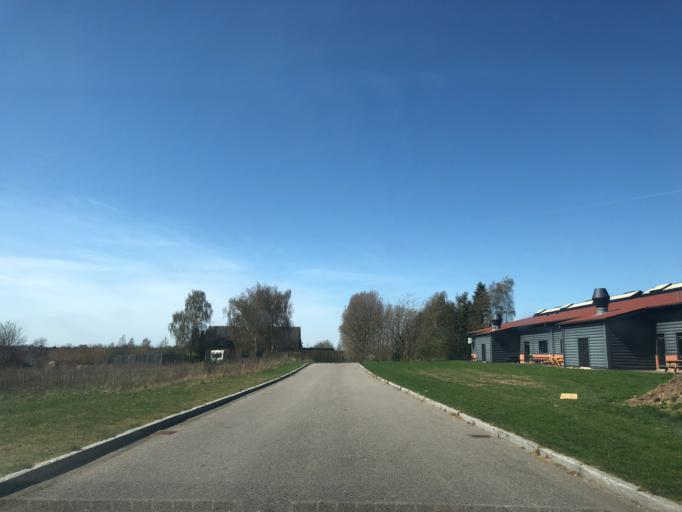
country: DK
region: Zealand
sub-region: Ringsted Kommune
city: Ringsted
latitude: 55.4261
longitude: 11.7849
